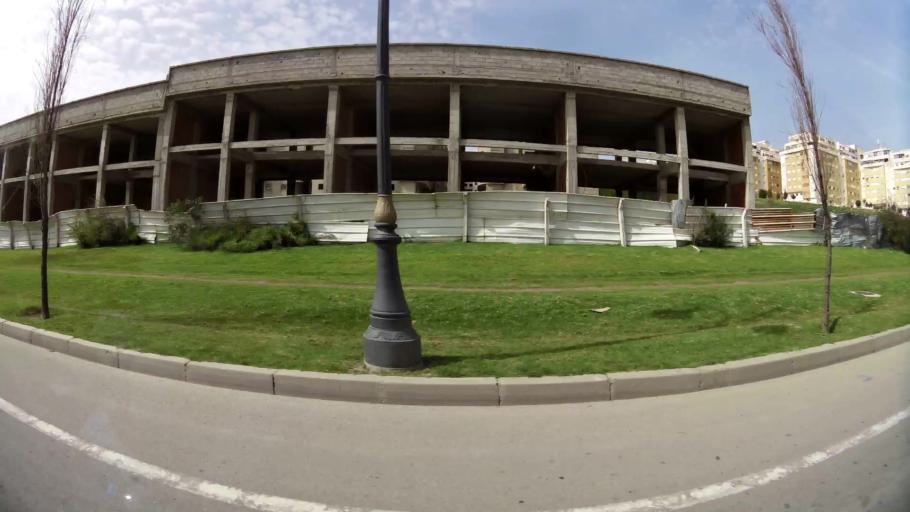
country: MA
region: Tanger-Tetouan
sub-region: Tanger-Assilah
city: Boukhalef
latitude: 35.7325
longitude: -5.8729
